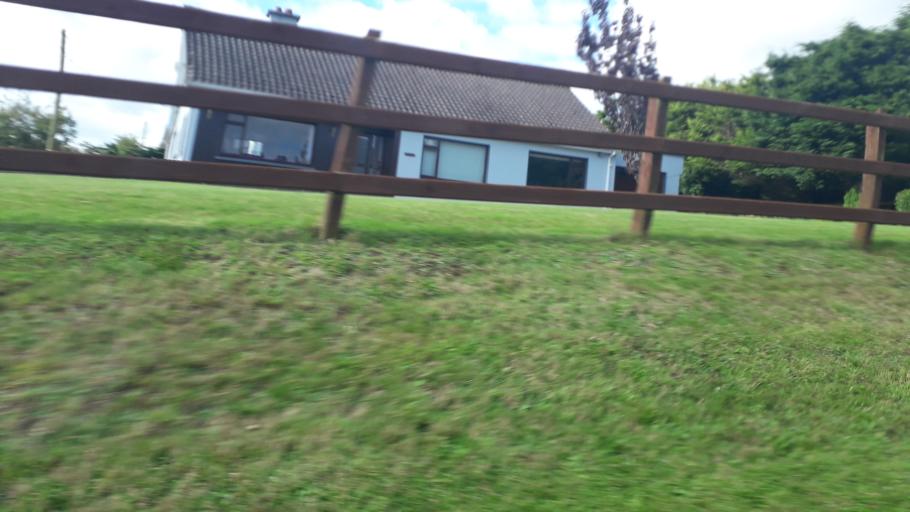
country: IE
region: Leinster
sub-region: Lu
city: Blackrock
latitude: 54.0202
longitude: -6.2957
